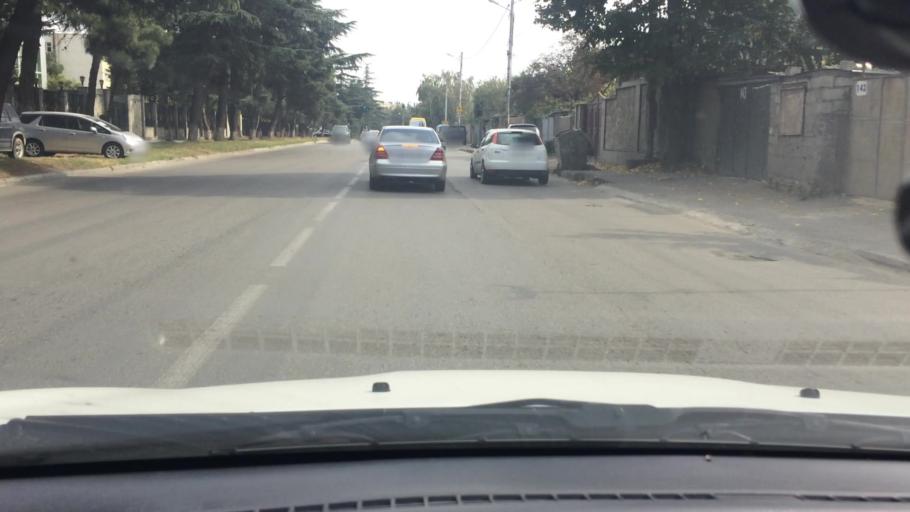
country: GE
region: T'bilisi
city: Tbilisi
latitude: 41.6553
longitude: 44.8999
